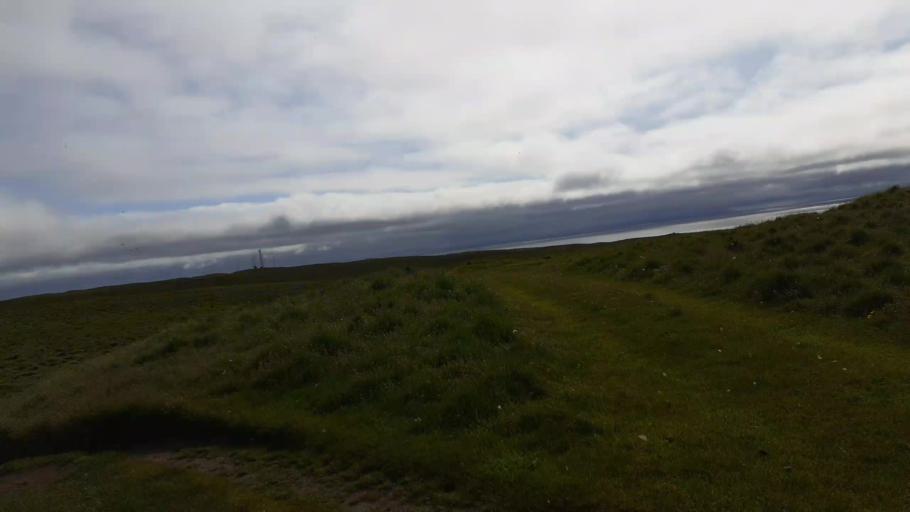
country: IS
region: Northeast
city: Dalvik
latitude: 66.5532
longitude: -17.9987
